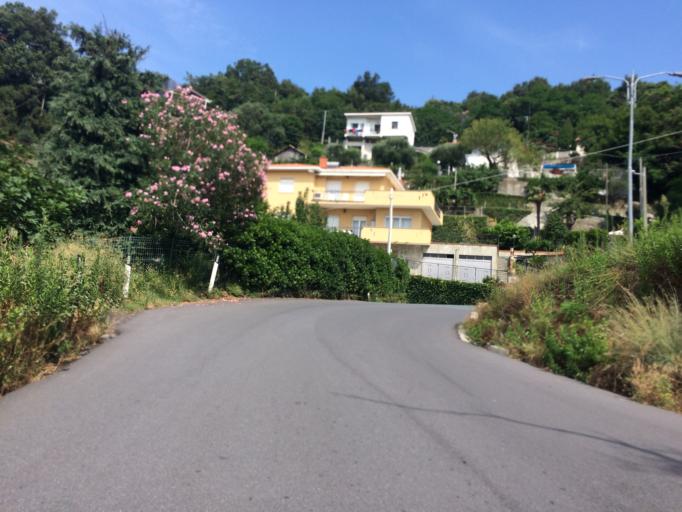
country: IT
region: Liguria
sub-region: Provincia di Savona
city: Varazze
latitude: 44.3790
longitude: 8.5700
